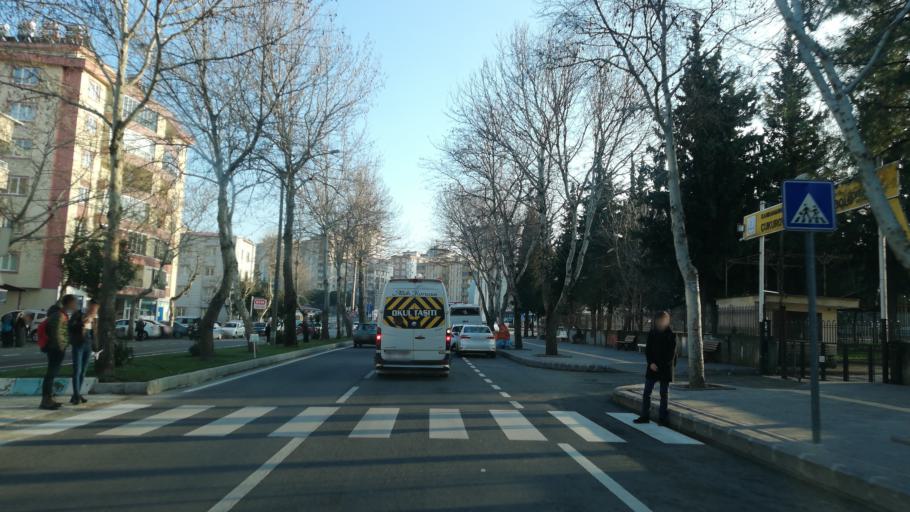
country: TR
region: Kahramanmaras
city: Kahramanmaras
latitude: 37.5861
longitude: 36.9041
